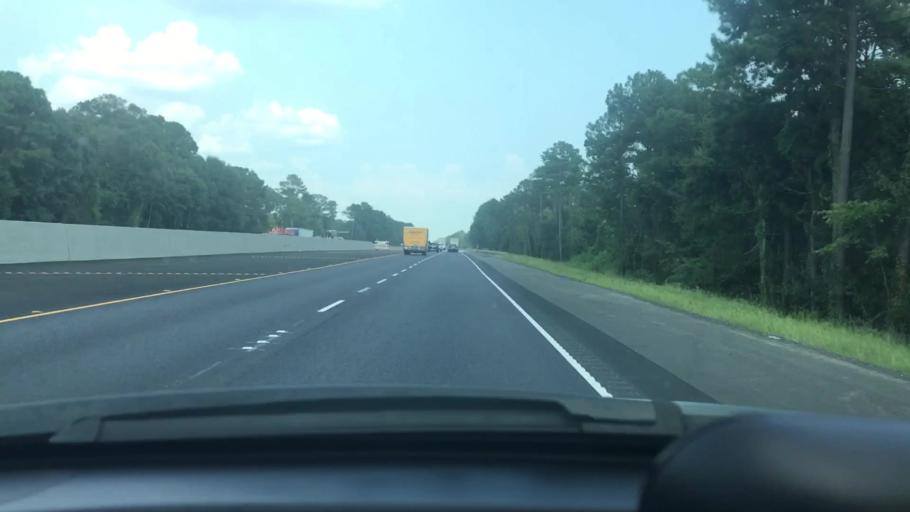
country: US
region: Louisiana
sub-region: Livingston Parish
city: Livingston
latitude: 30.4748
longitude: -90.6775
